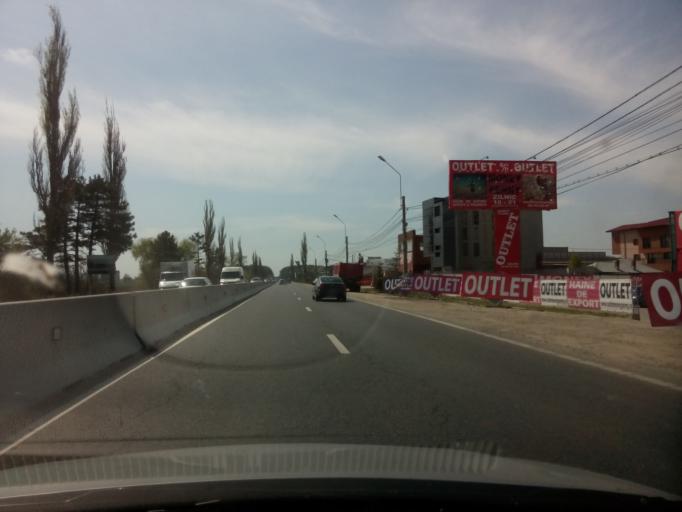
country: RO
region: Ilfov
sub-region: Comuna Corbeanca
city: Corbeanca
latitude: 44.5976
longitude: 26.0713
